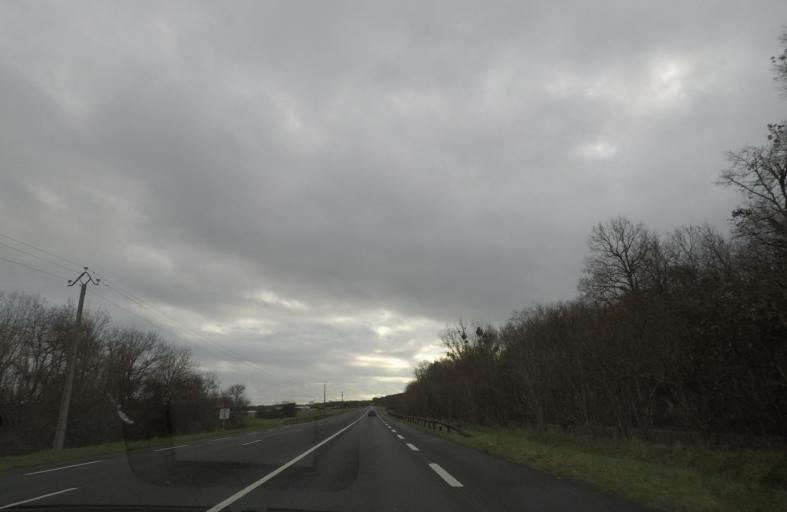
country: FR
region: Centre
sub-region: Departement du Loir-et-Cher
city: Soings-en-Sologne
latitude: 47.4451
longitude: 1.5413
